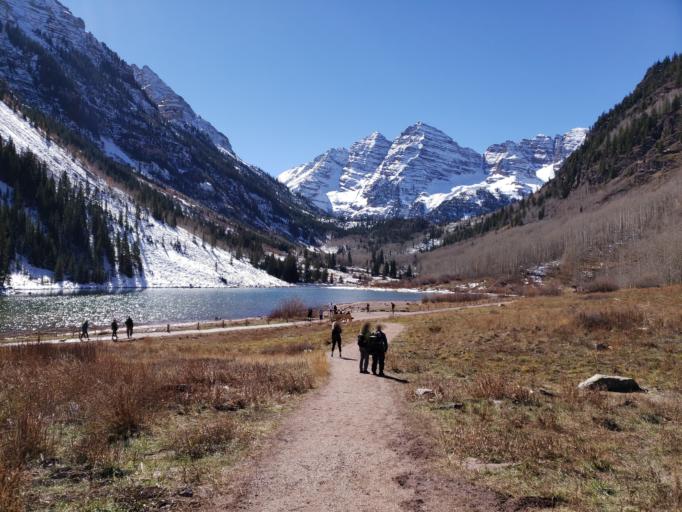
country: US
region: Colorado
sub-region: Pitkin County
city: Snowmass Village
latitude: 39.0987
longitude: -106.9435
